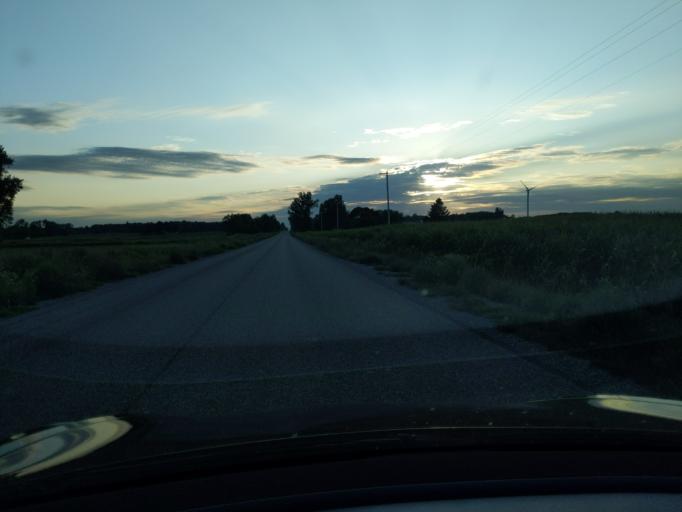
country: US
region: Michigan
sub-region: Gratiot County
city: Saint Louis
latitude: 43.3788
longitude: -84.5691
